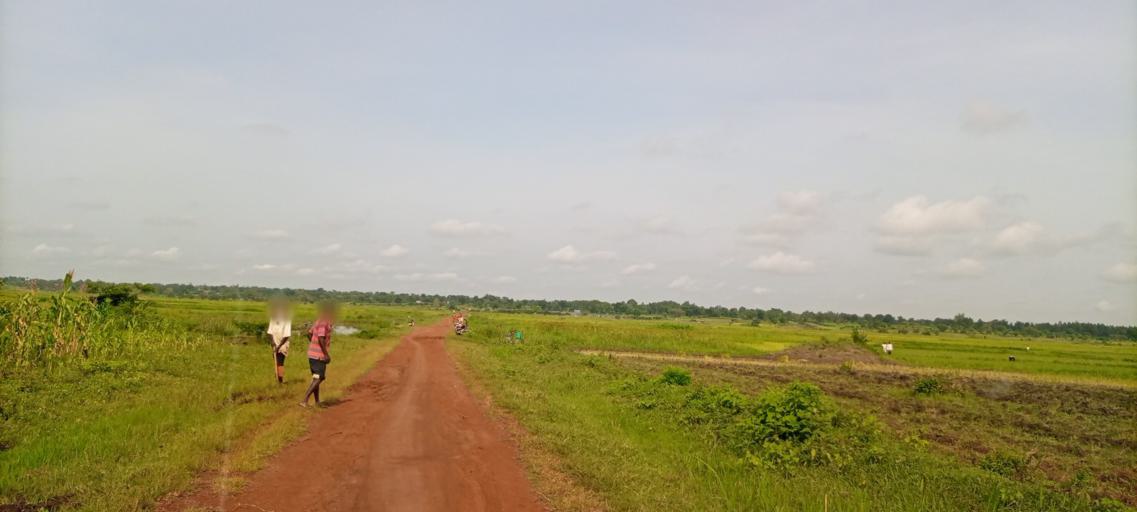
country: UG
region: Eastern Region
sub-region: Kibuku District
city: Kibuku
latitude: 1.1013
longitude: 33.7770
